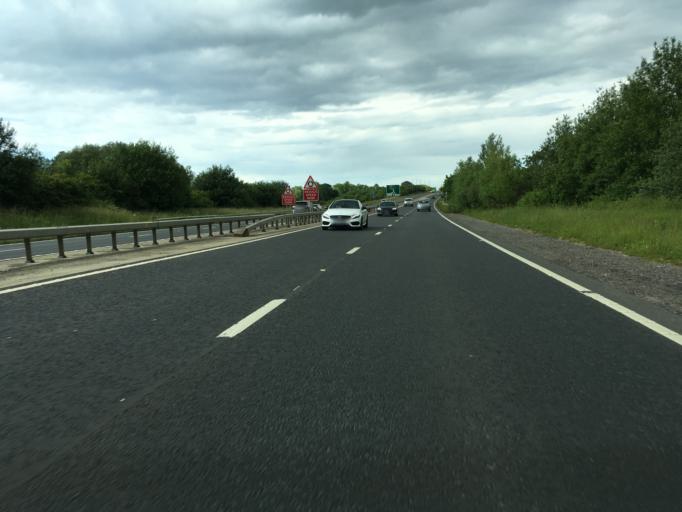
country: GB
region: England
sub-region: Central Bedfordshire
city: Leighton Buzzard
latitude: 51.9224
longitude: -0.6990
